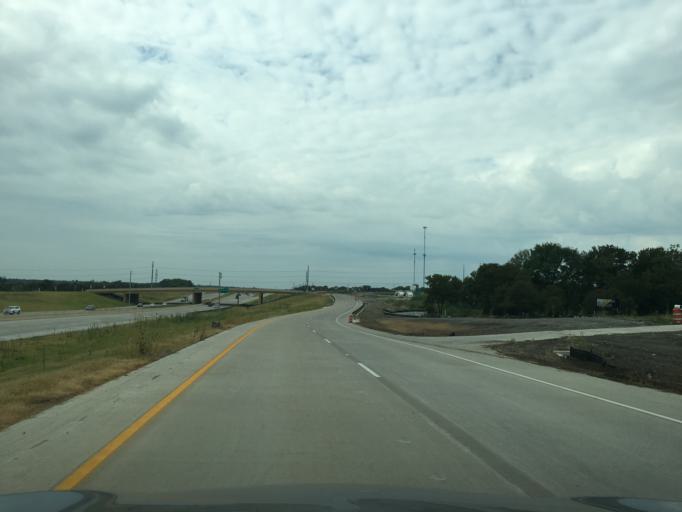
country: US
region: Texas
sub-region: Collin County
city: Melissa
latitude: 33.3223
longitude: -96.5907
